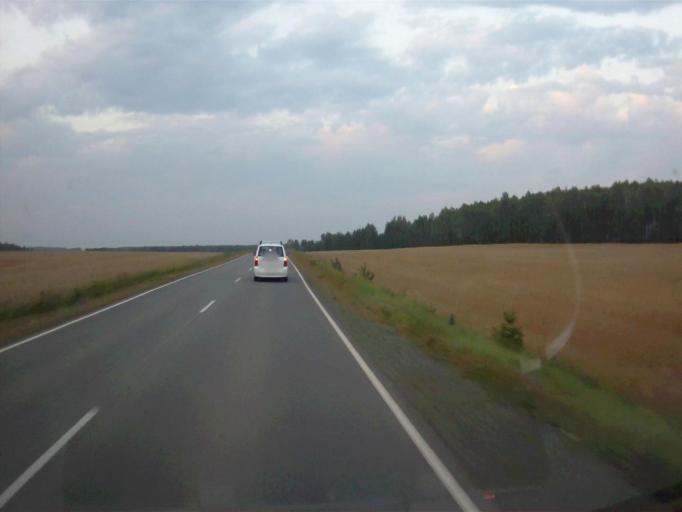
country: RU
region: Chelyabinsk
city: Chebarkul'
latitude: 55.1707
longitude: 60.4509
